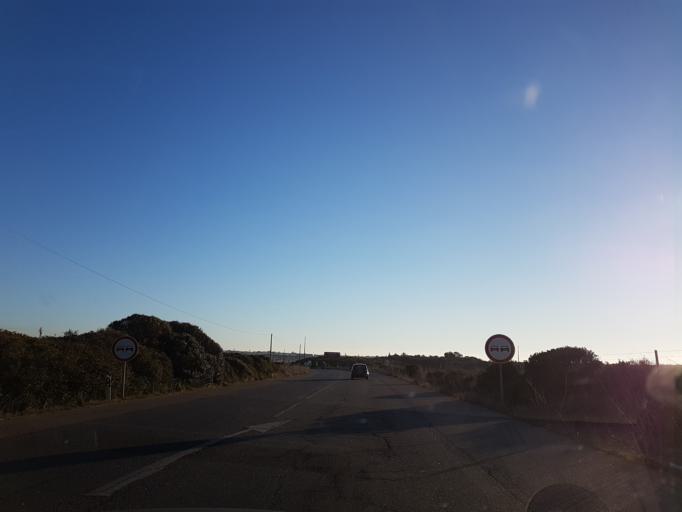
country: PT
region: Faro
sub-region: Vila do Bispo
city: Sagres
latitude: 37.0262
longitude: -8.9375
